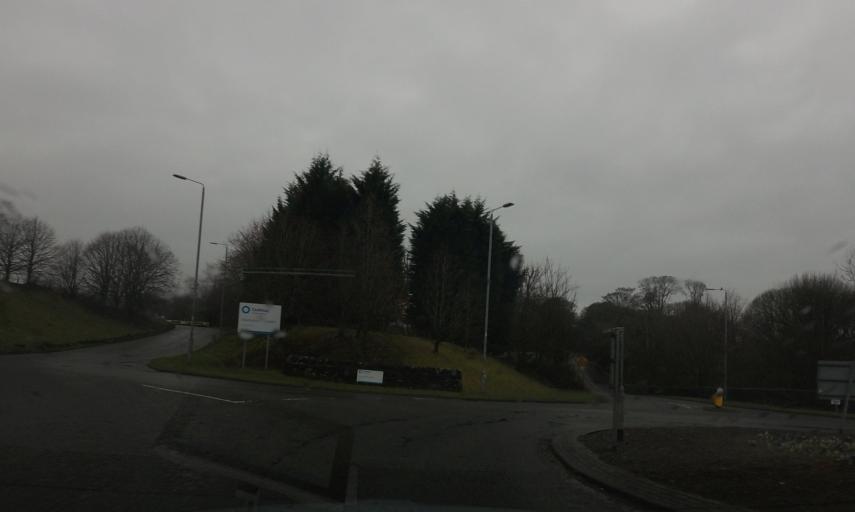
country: GB
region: Scotland
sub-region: East Dunbartonshire
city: Milngavie
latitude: 55.9421
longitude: -4.3491
